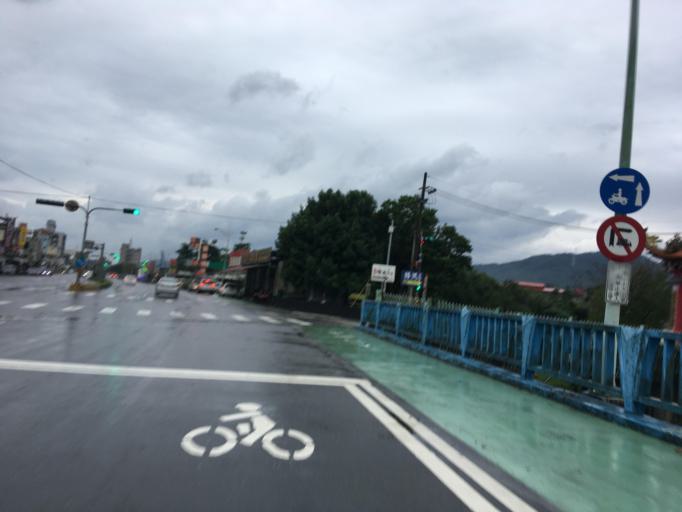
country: TW
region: Taiwan
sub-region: Yilan
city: Yilan
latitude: 24.6344
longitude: 121.7885
